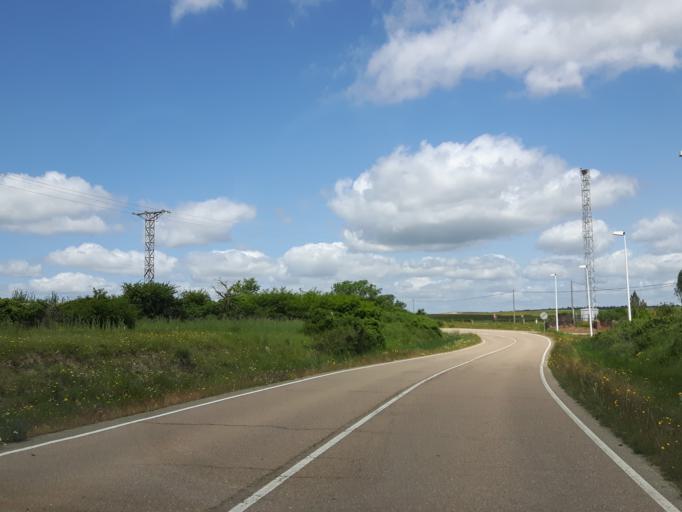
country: ES
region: Castille and Leon
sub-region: Provincia de Salamanca
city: Villar de la Yegua
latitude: 40.7241
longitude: -6.7062
